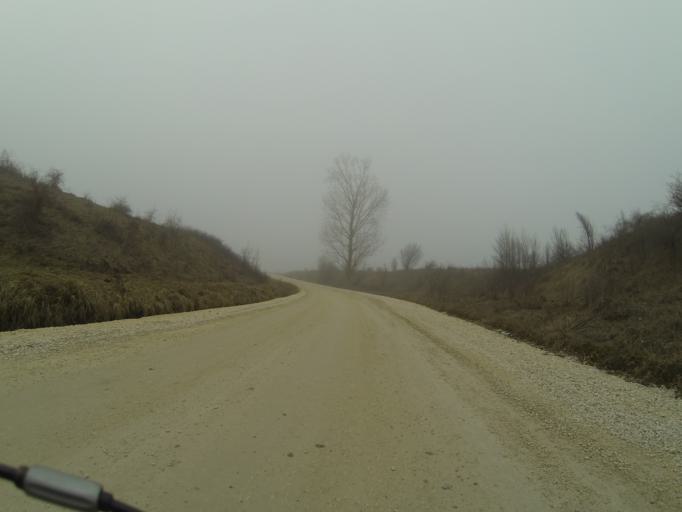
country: RO
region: Mehedinti
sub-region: Comuna Balacita
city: Gvardinita
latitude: 44.4108
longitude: 23.1428
